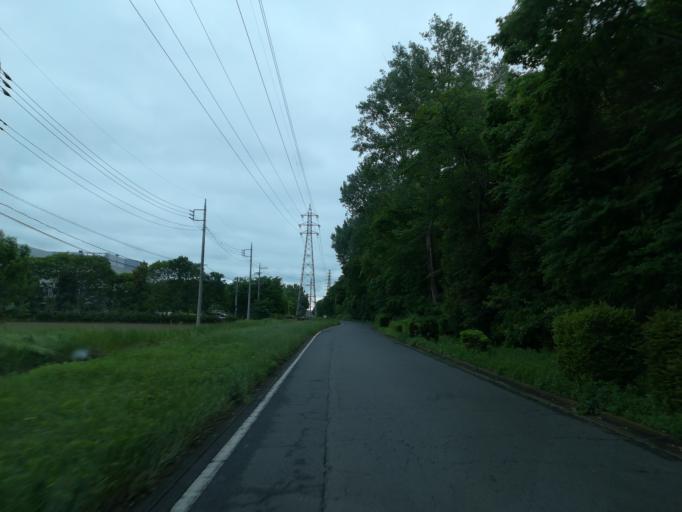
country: JP
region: Ibaraki
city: Tsukuba
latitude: 36.1163
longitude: 140.0921
